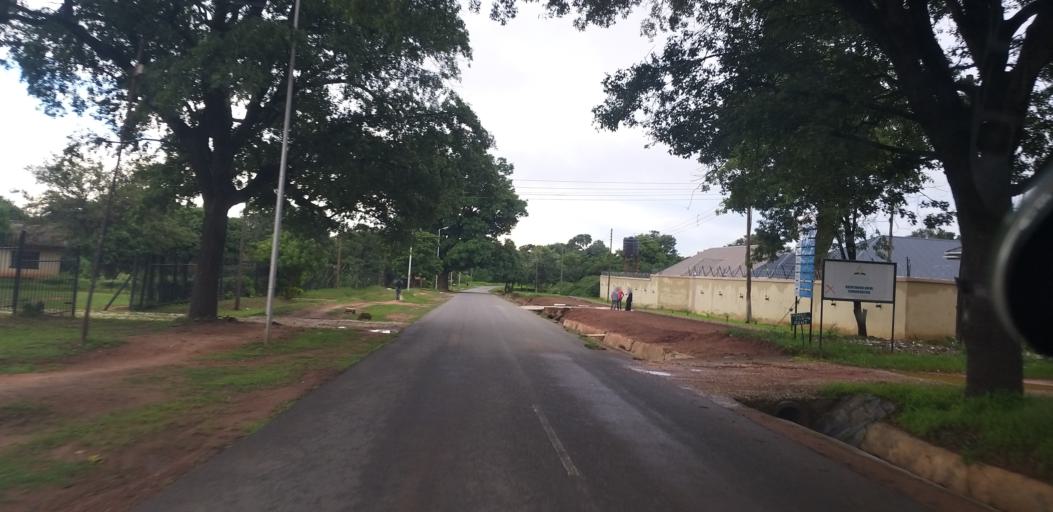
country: ZM
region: Lusaka
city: Lusaka
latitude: -15.4307
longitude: 28.3320
